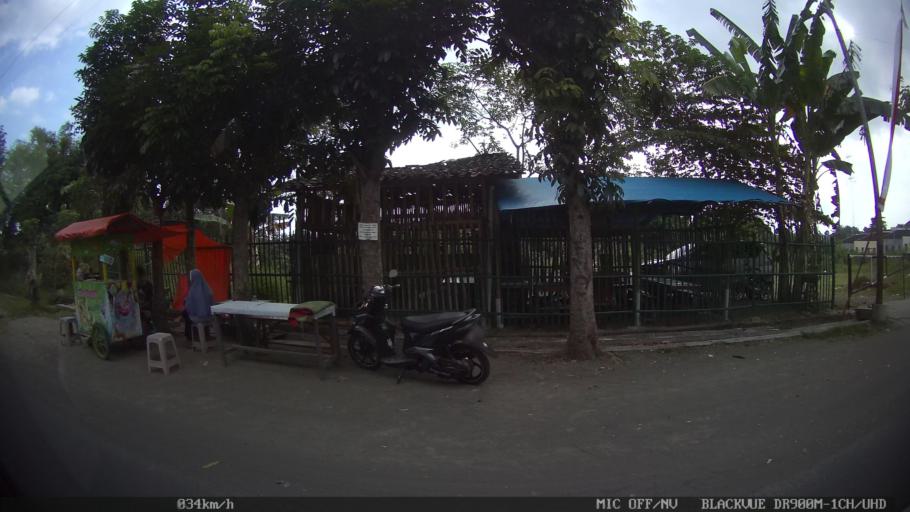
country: ID
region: Daerah Istimewa Yogyakarta
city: Gamping Lor
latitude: -7.7868
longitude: 110.3417
